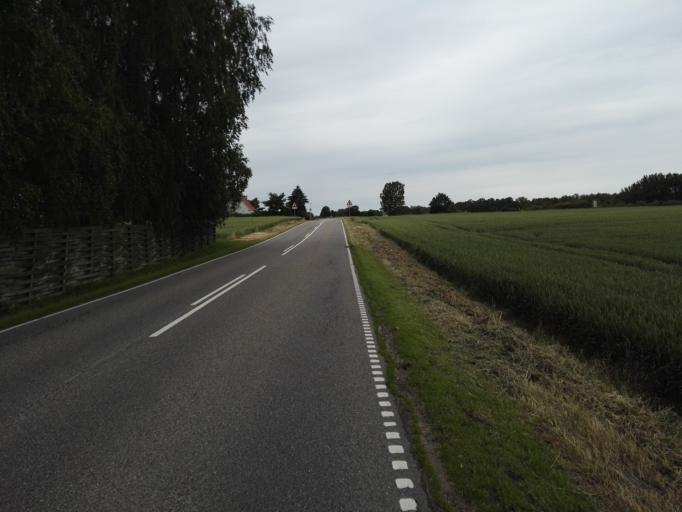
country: DK
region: Zealand
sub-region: Roskilde Kommune
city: Jyllinge
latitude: 55.7828
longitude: 12.1184
